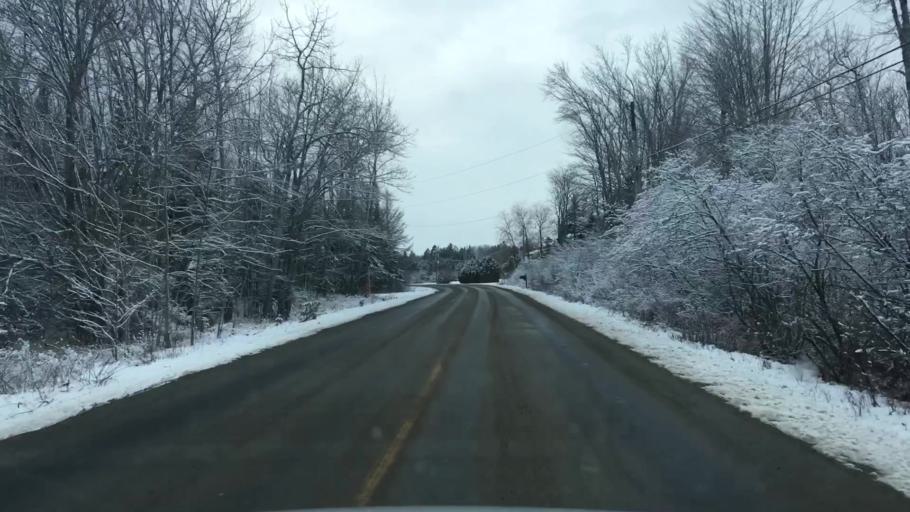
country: US
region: Maine
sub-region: Knox County
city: Owls Head
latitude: 44.0693
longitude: -69.0760
